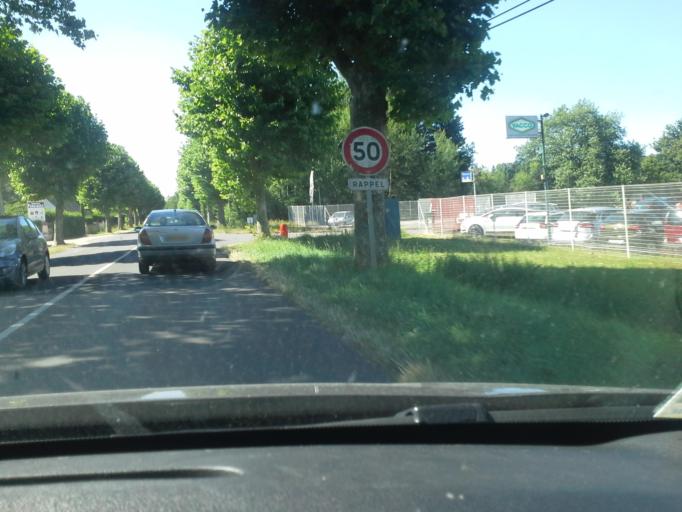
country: FR
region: Centre
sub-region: Departement du Loir-et-Cher
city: Cellettes
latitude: 47.5202
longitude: 1.3938
